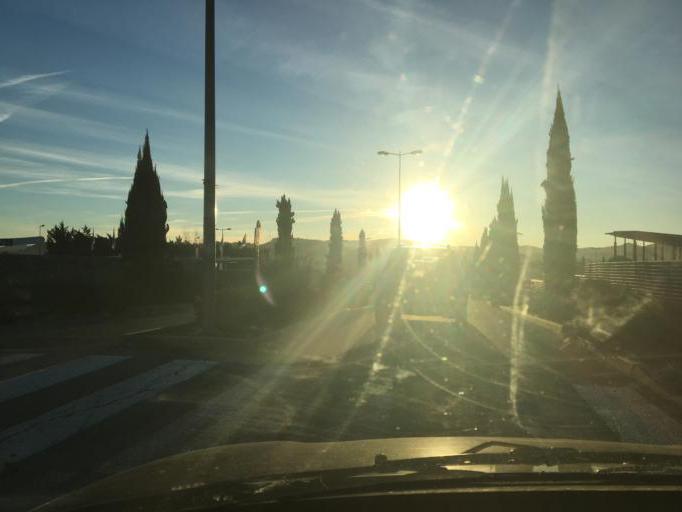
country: FR
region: Provence-Alpes-Cote d'Azur
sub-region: Departement du Var
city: Les Arcs
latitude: 43.4524
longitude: 6.4899
